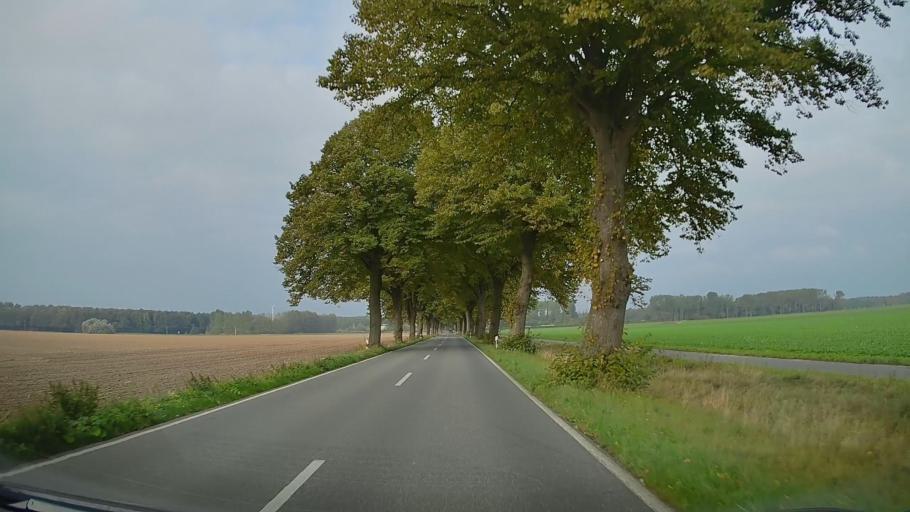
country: DE
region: Mecklenburg-Vorpommern
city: Bad Doberan
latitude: 54.1321
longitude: 11.8343
